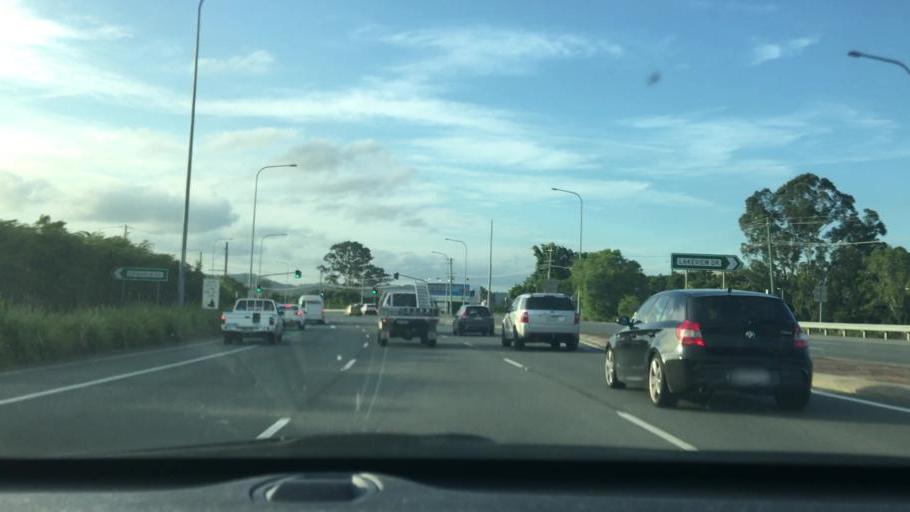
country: AU
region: Queensland
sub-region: Gold Coast
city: Nerang
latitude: -28.0018
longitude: 153.3610
